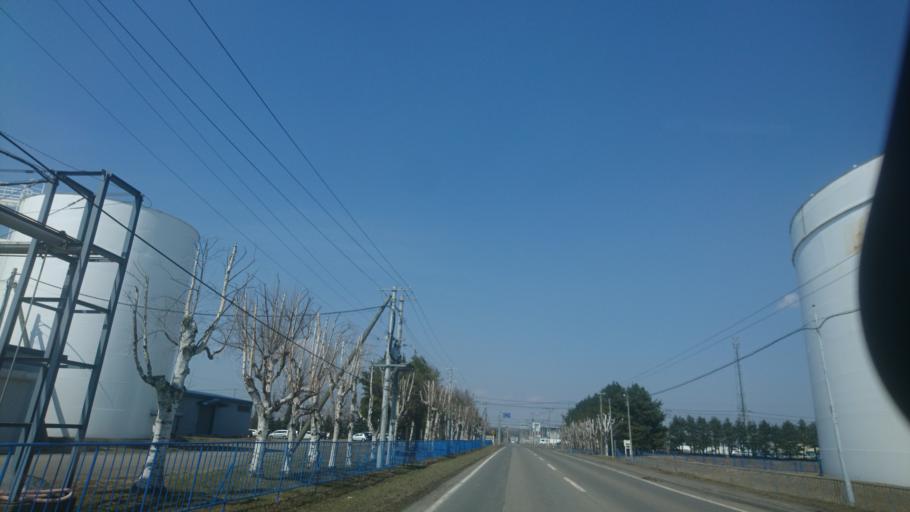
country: JP
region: Hokkaido
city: Obihiro
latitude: 42.9217
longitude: 143.0825
